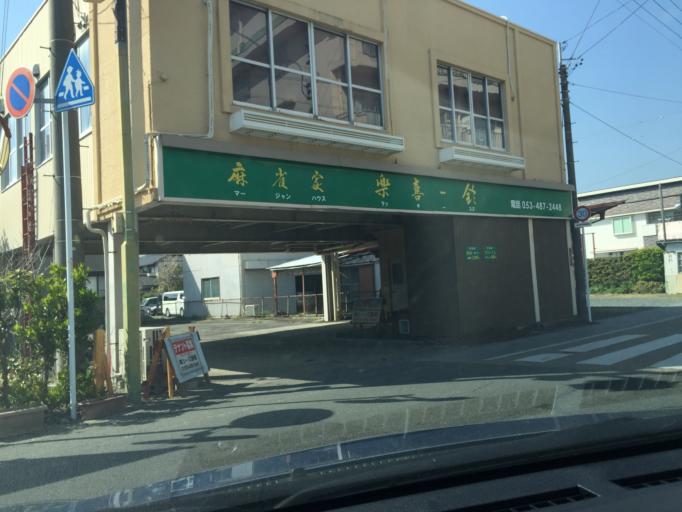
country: JP
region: Shizuoka
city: Kosai-shi
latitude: 34.7643
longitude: 137.6136
